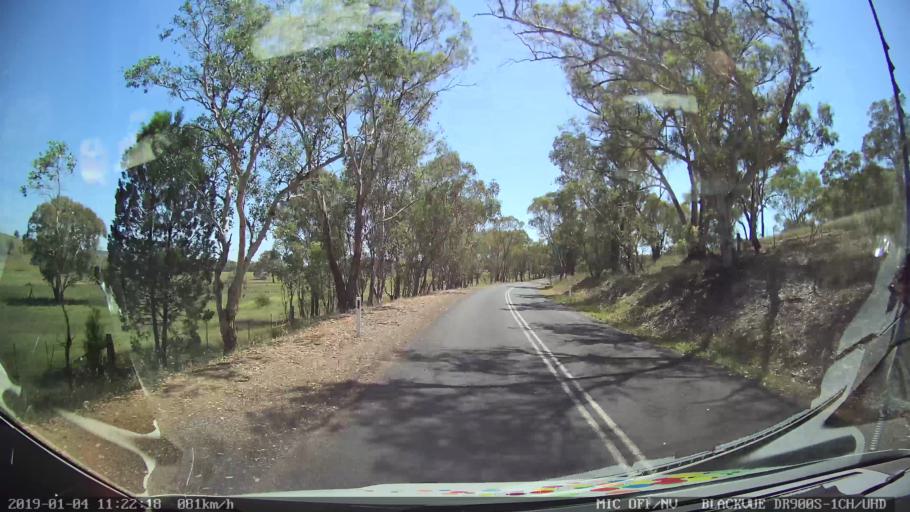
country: AU
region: New South Wales
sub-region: Cabonne
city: Molong
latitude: -33.1468
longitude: 148.7199
